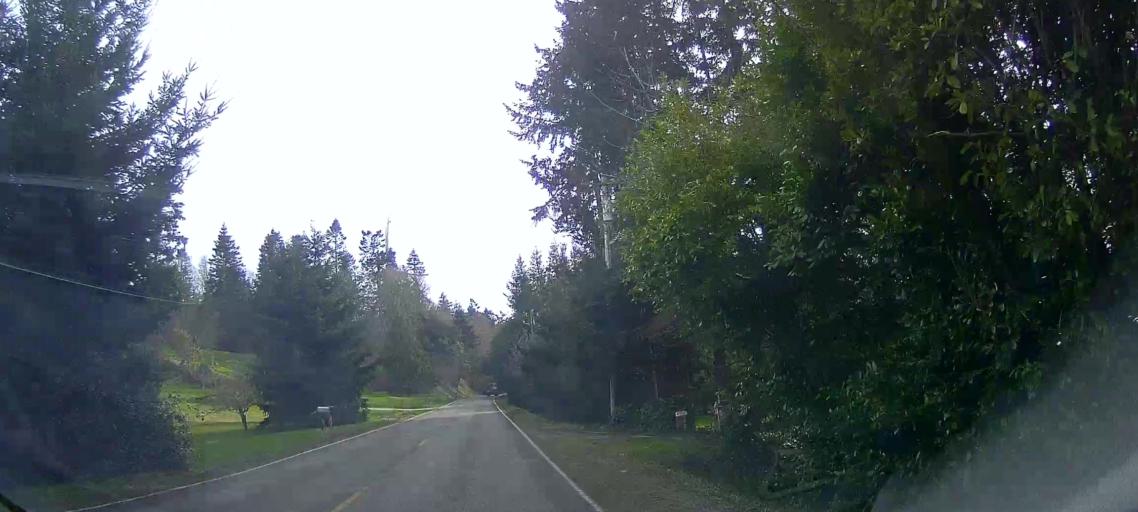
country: US
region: Washington
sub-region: Island County
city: Langley
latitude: 48.0792
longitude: -122.3919
